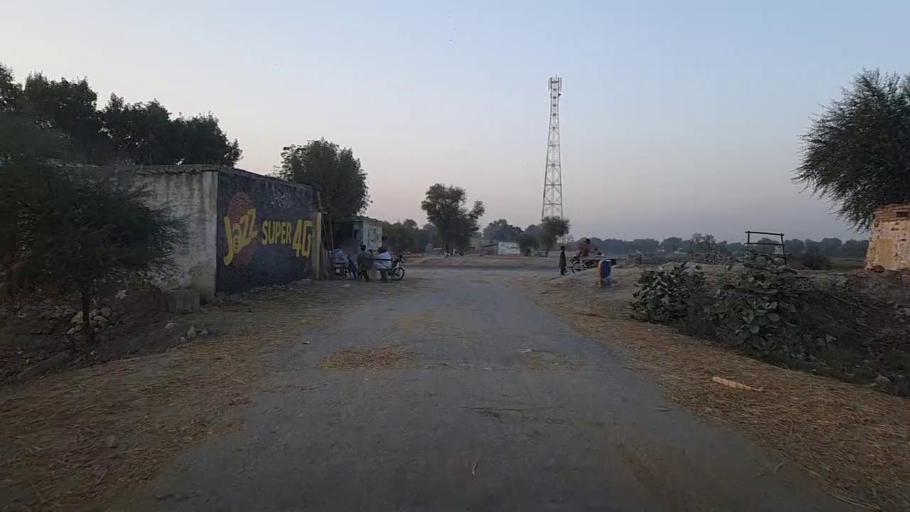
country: PK
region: Sindh
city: Kashmor
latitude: 28.4175
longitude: 69.4503
